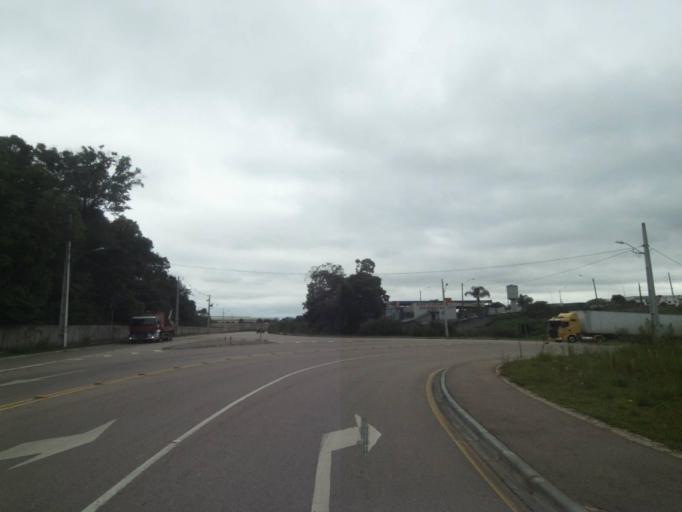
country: BR
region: Parana
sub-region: Sao Jose Dos Pinhais
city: Sao Jose dos Pinhais
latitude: -25.5548
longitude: -49.3043
